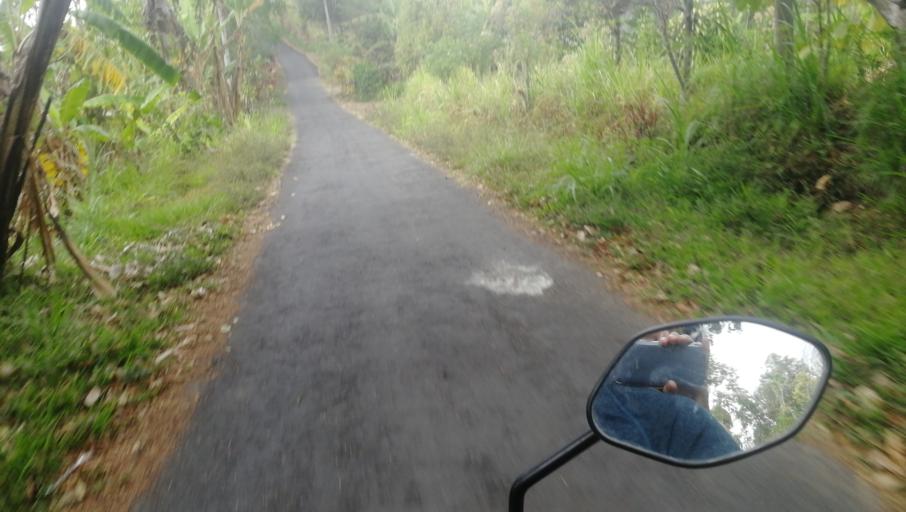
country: ID
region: Bali
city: Banjar Ambengan
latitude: -8.2158
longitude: 115.1099
